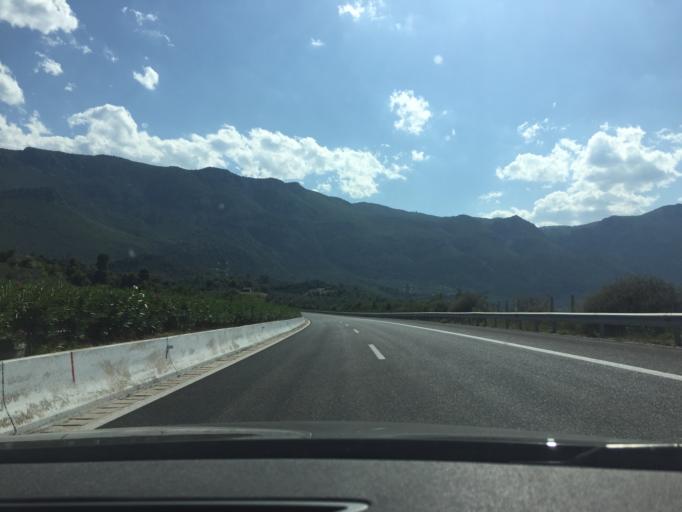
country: GR
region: Central Greece
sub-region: Nomos Fthiotidos
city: Ayios Konstandinos
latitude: 38.7552
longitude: 22.8839
